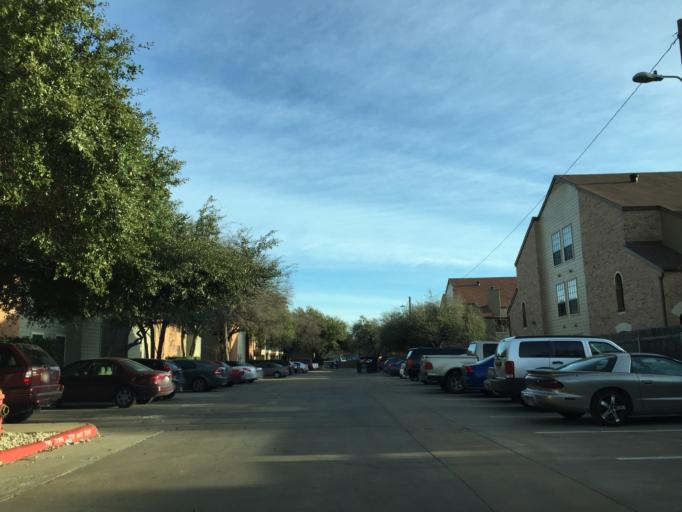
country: US
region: Texas
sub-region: Williamson County
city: Jollyville
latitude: 30.4105
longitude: -97.7438
